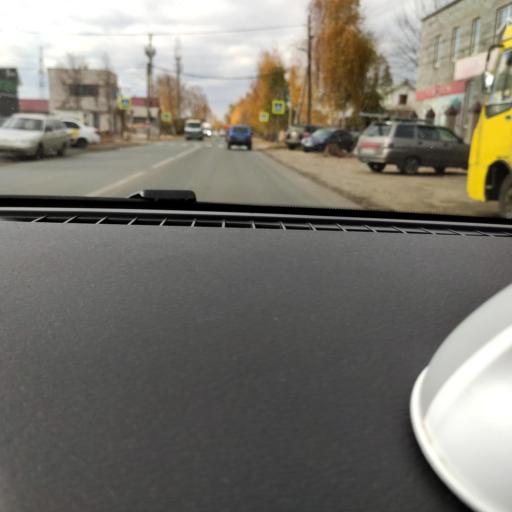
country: RU
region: Samara
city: Petra-Dubrava
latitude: 53.2530
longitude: 50.3233
